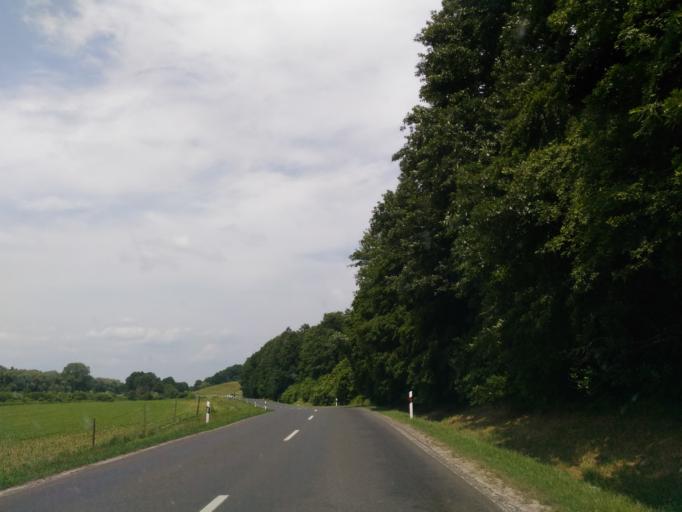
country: HU
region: Baranya
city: Komlo
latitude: 46.1663
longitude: 18.2155
